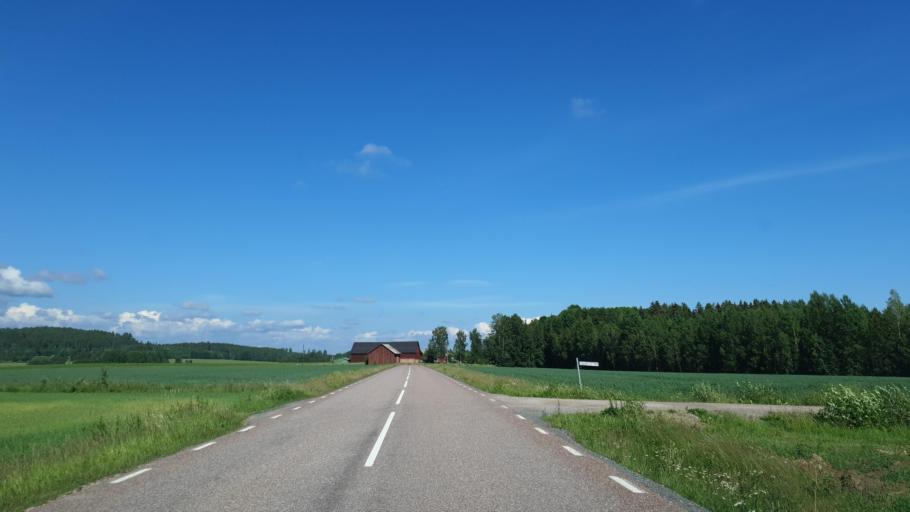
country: SE
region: Dalarna
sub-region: Saters Kommun
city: Saeter
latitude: 60.3999
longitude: 15.8561
